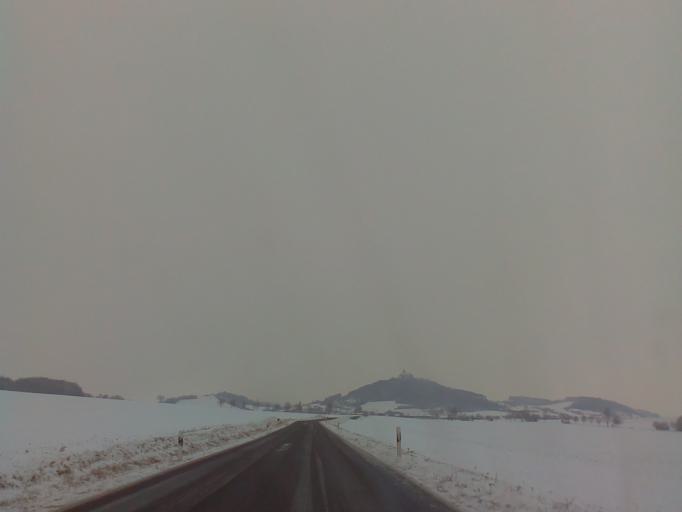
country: DE
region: Thuringia
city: Arnstadt
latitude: 50.8452
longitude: 10.9049
